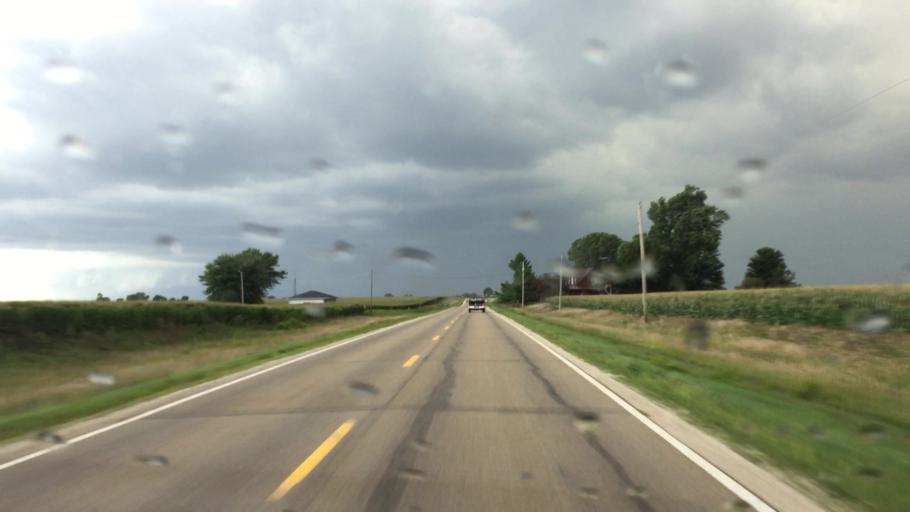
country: US
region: Iowa
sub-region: Henry County
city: New London
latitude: 40.7843
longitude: -91.5094
